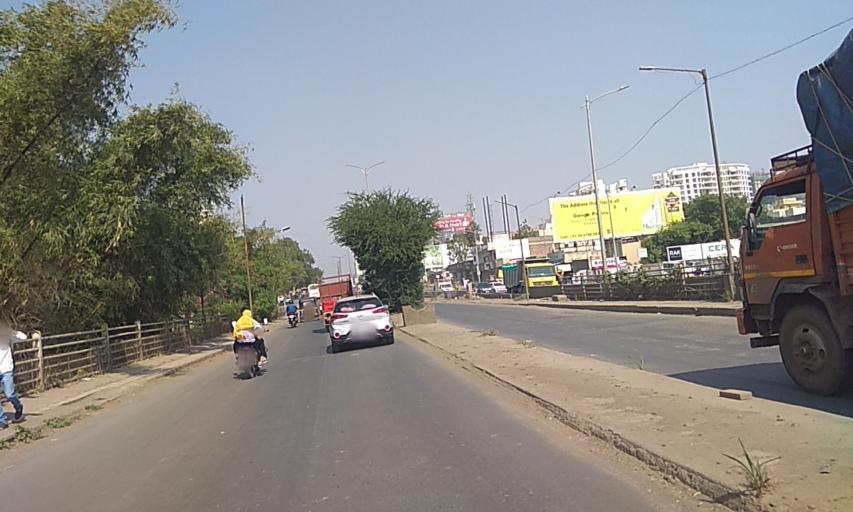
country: IN
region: Maharashtra
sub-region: Pune Division
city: Lohogaon
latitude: 18.5369
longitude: 73.9340
